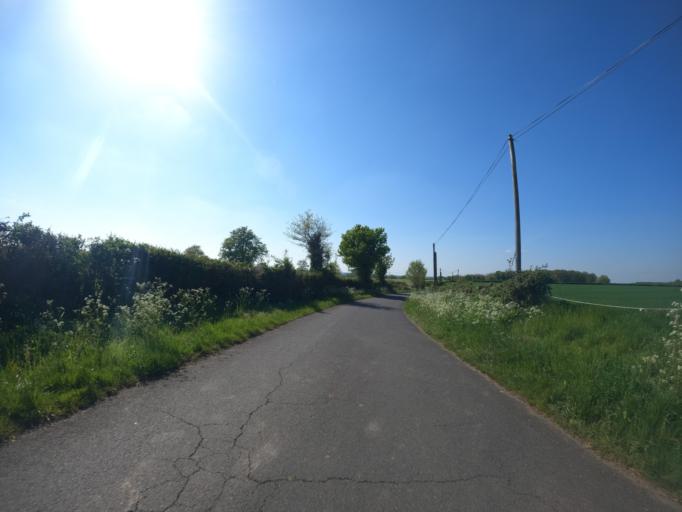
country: FR
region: Poitou-Charentes
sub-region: Departement des Deux-Sevres
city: Moncoutant
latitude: 46.6836
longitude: -0.5304
